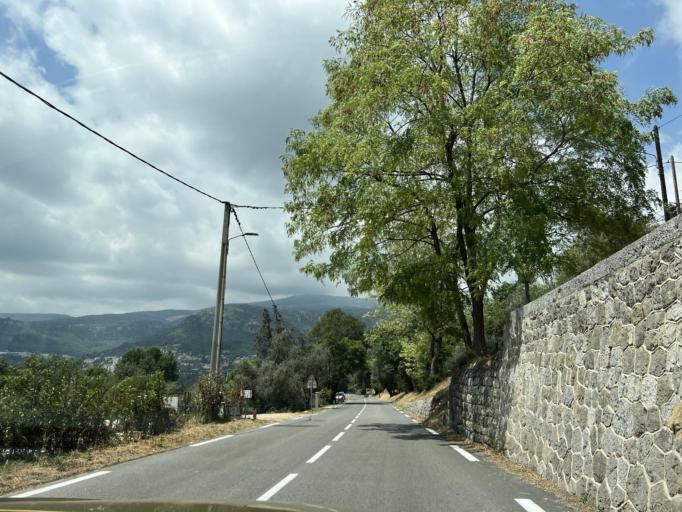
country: FR
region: Provence-Alpes-Cote d'Azur
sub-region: Departement des Alpes-Maritimes
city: Le Rouret
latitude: 43.7035
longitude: 7.0161
